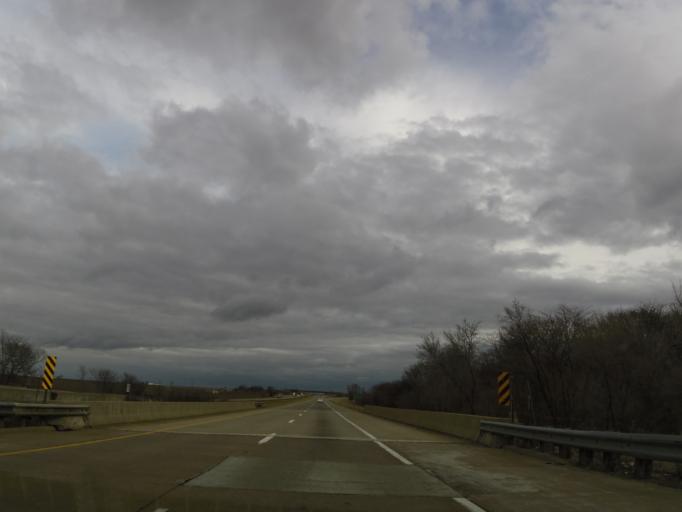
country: US
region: Iowa
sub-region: Black Hawk County
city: Elk Run Heights
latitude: 42.4197
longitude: -92.1812
